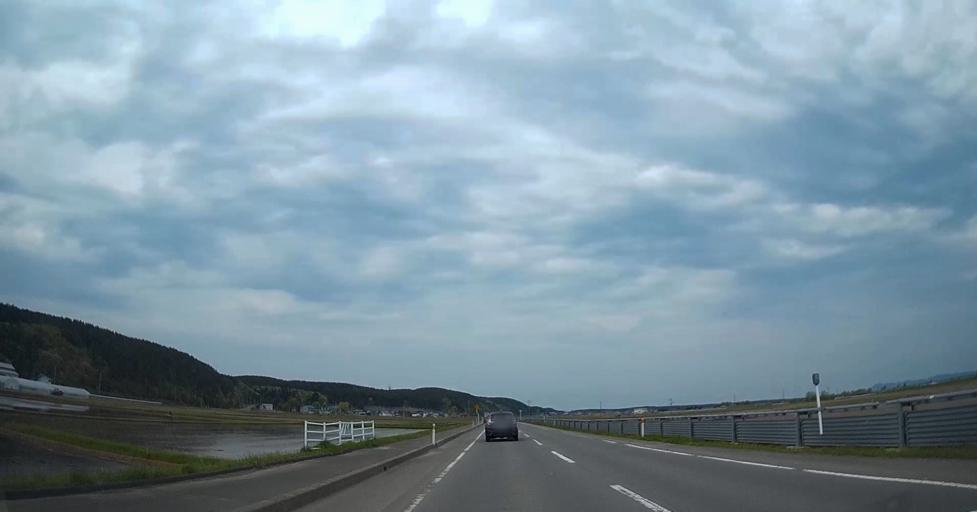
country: JP
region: Aomori
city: Shimokizukuri
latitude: 40.9920
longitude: 140.3655
